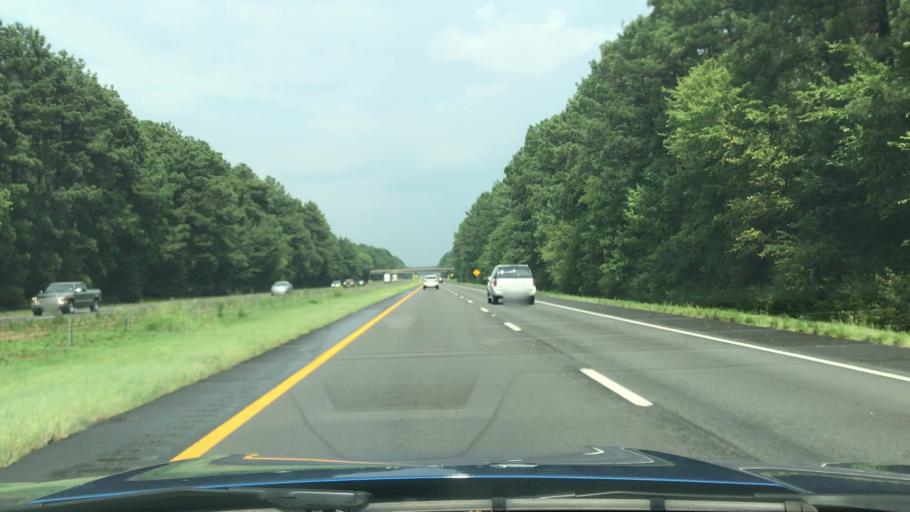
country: US
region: Texas
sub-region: Harrison County
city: Hallsville
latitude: 32.4792
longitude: -94.5501
